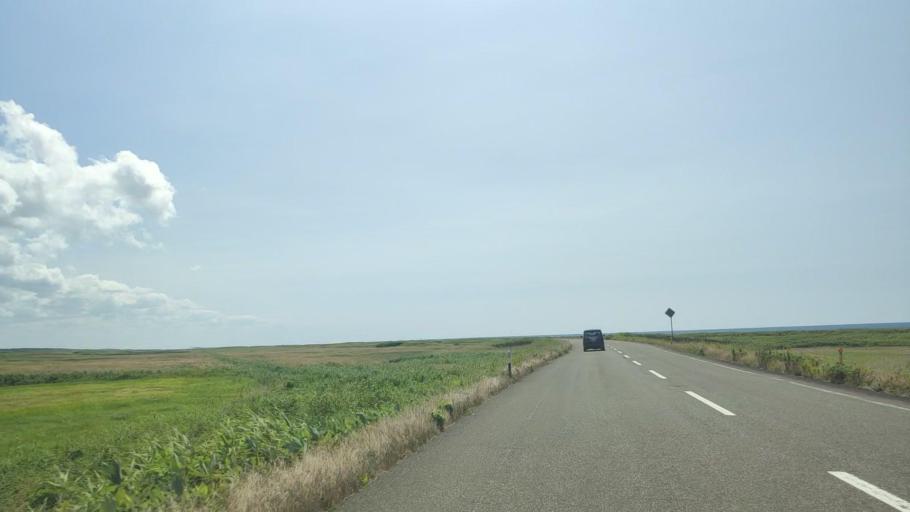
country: JP
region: Hokkaido
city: Wakkanai
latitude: 45.1260
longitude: 141.6077
